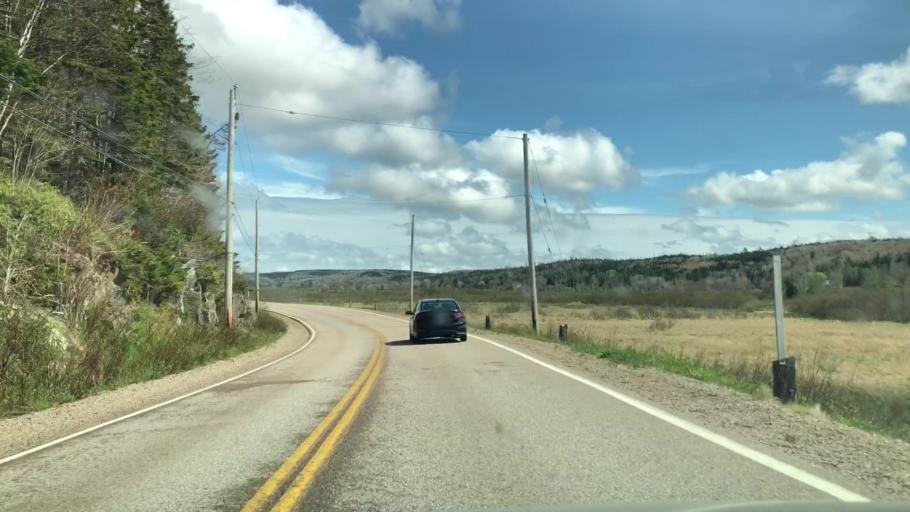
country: CA
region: Nova Scotia
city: Antigonish
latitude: 45.1963
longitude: -62.0012
